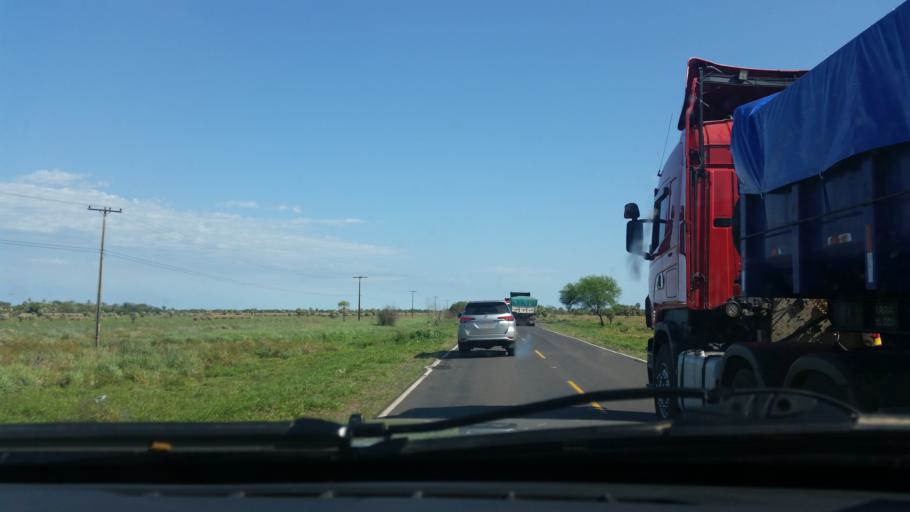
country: PY
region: Presidente Hayes
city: Benjamin Aceval
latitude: -24.6770
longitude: -57.9809
